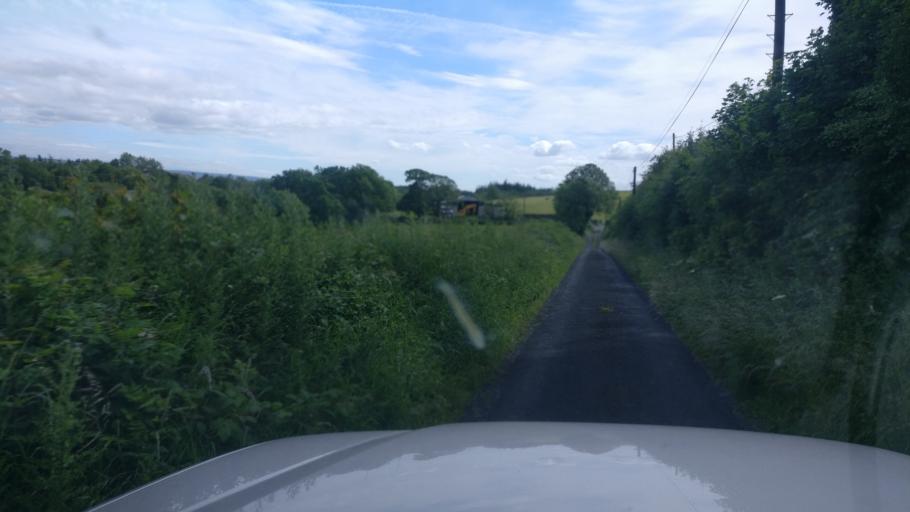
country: IE
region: Connaught
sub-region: County Galway
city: Gort
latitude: 53.0771
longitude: -8.7729
